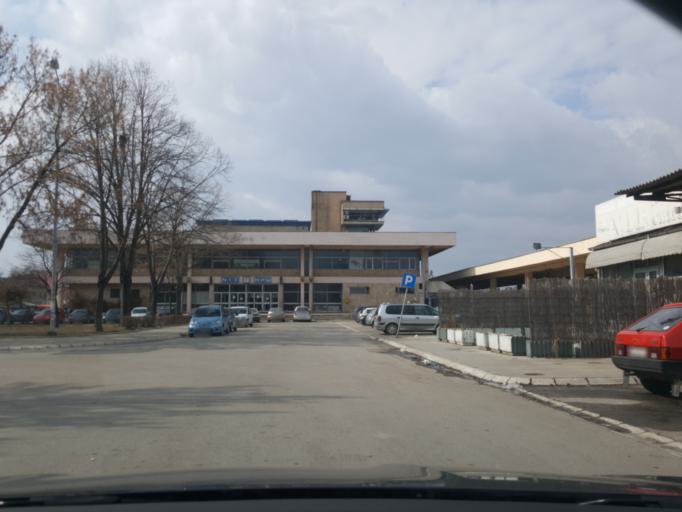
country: RS
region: Central Serbia
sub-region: Nisavski Okrug
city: Nis
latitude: 43.3162
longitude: 21.8786
